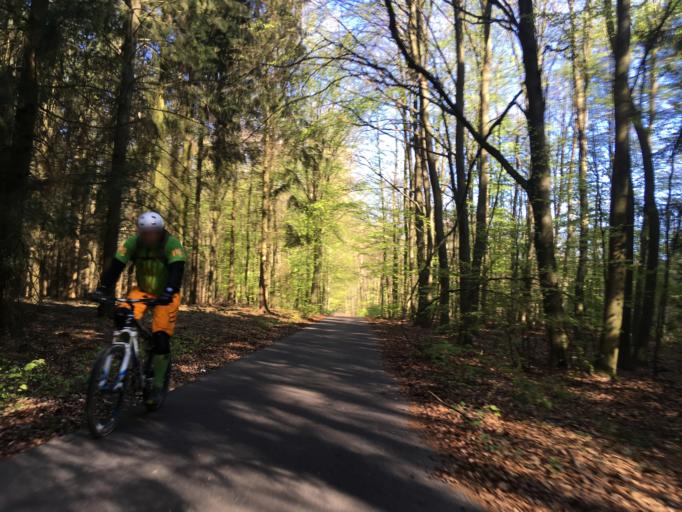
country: DE
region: Brandenburg
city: Wandlitz
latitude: 52.7337
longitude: 13.5035
